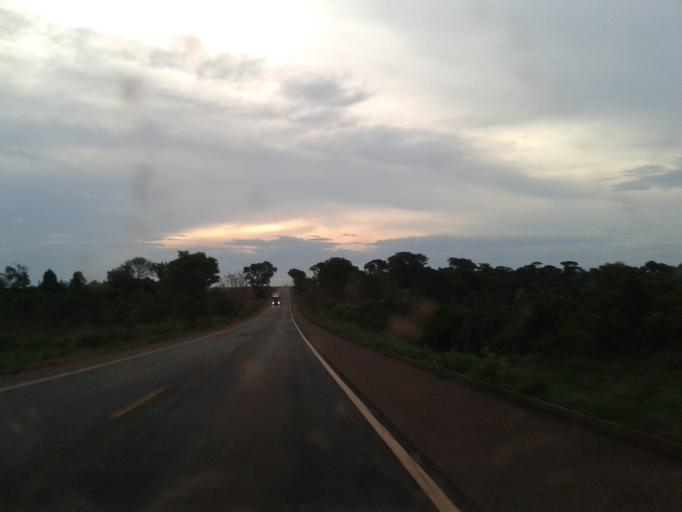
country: BR
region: Goias
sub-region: Santa Helena De Goias
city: Santa Helena de Goias
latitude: -17.8835
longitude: -50.6910
